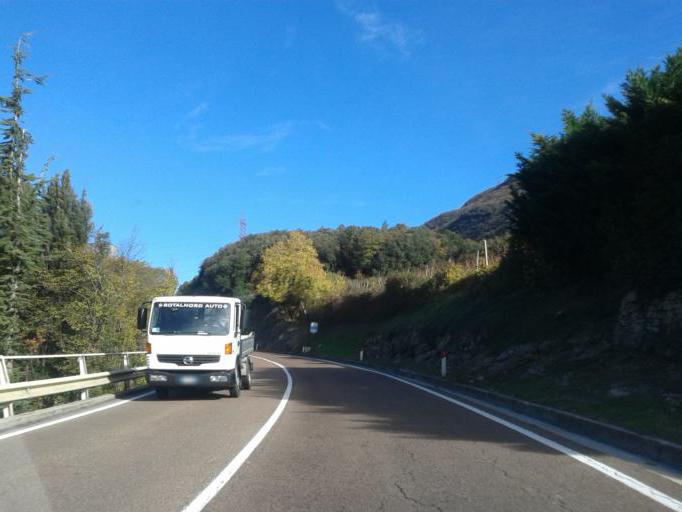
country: IT
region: Trentino-Alto Adige
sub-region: Provincia di Trento
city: Padergnone
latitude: 46.0627
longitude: 10.9875
